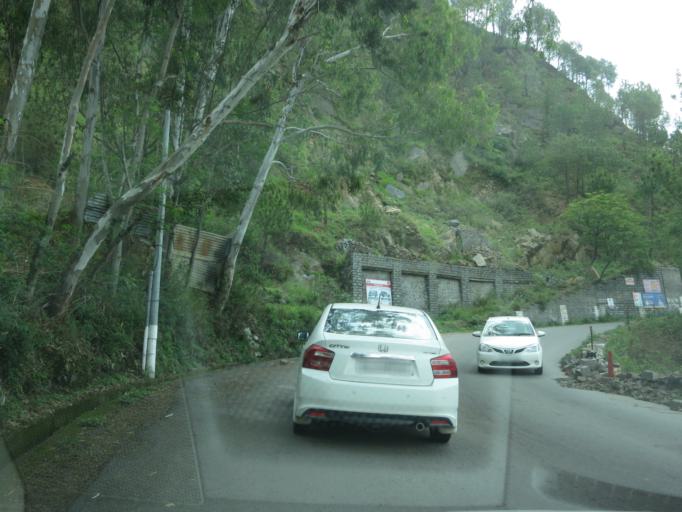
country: IN
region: Himachal Pradesh
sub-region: Solan
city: Dagshai
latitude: 30.8894
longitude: 77.0708
